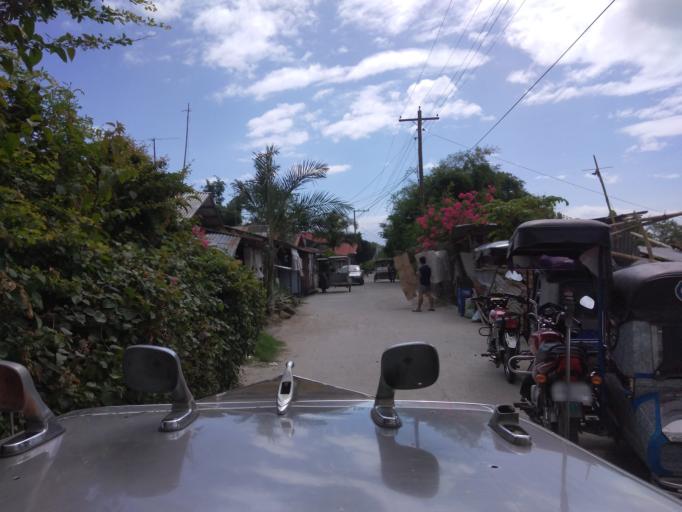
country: PH
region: Central Luzon
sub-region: Province of Pampanga
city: Anao
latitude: 15.1190
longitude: 120.7014
